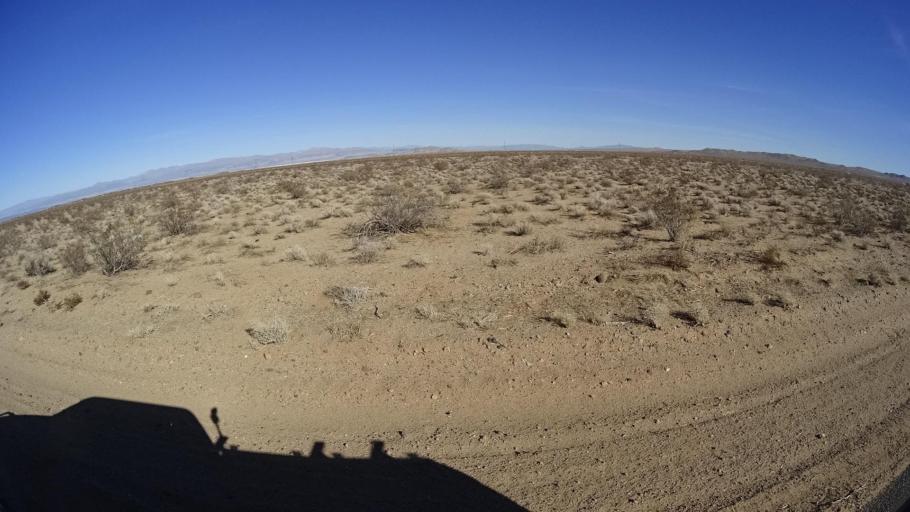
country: US
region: California
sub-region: Kern County
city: China Lake Acres
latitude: 35.5798
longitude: -117.7866
